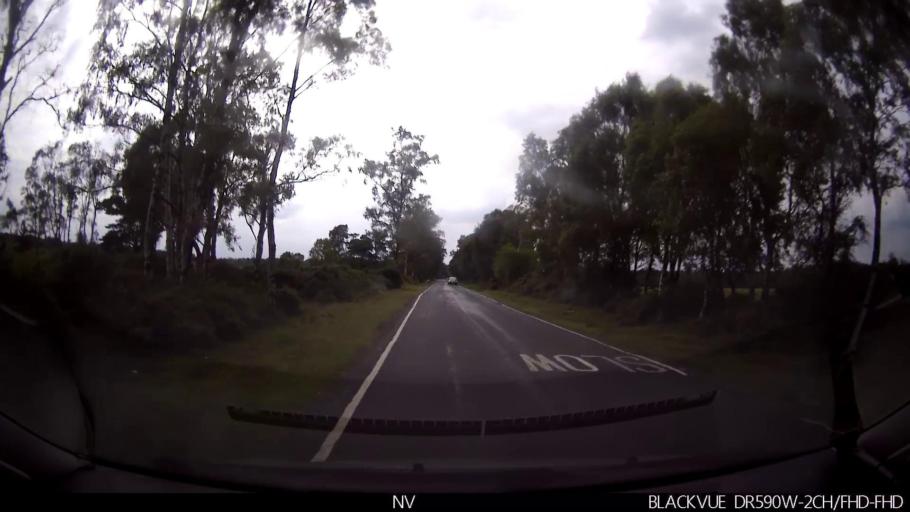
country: GB
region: England
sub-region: North Yorkshire
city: Strensall
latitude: 54.0470
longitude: -0.9970
